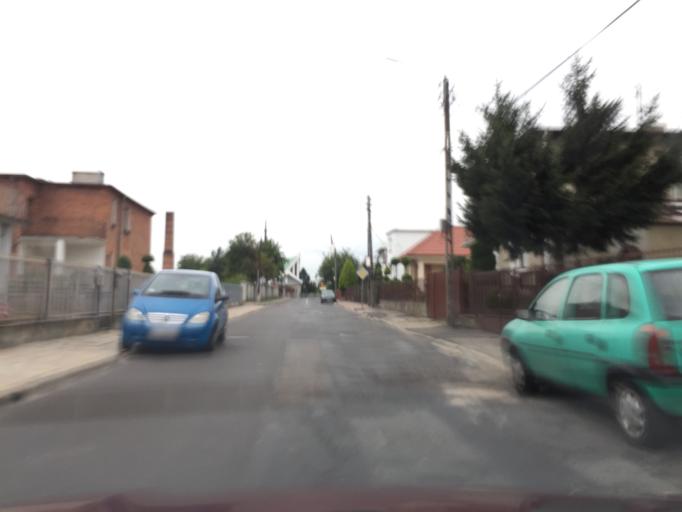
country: PL
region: Greater Poland Voivodeship
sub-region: Kalisz
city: Kalisz
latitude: 51.7767
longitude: 18.0869
